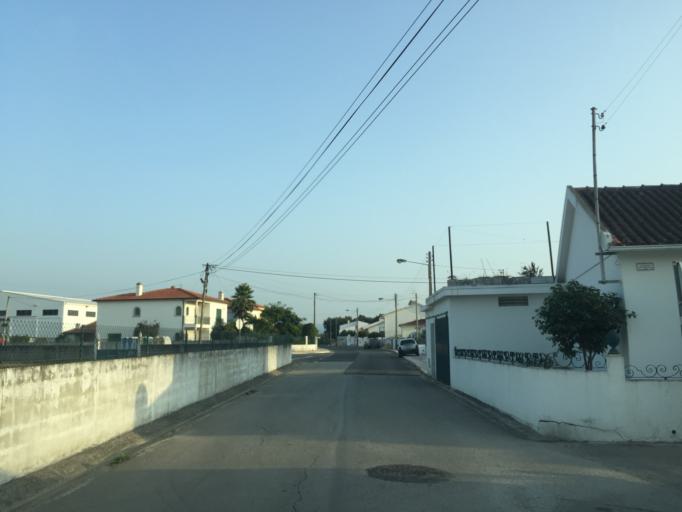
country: PT
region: Leiria
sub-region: Batalha
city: Batalha
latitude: 39.6629
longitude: -8.8327
